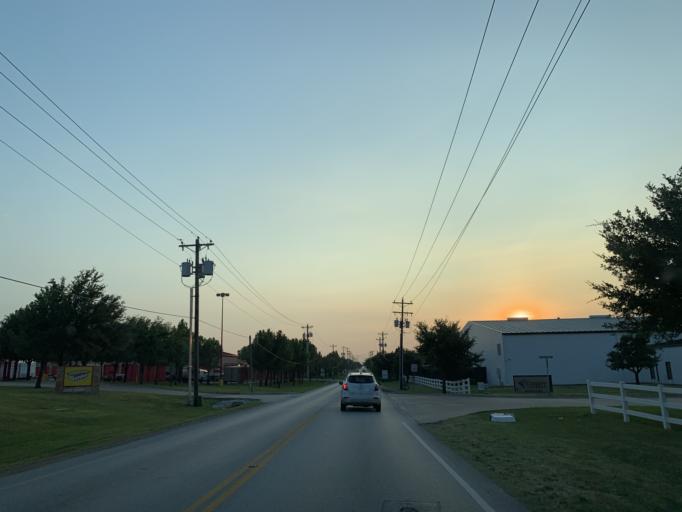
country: US
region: Texas
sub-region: Tarrant County
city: Keller
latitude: 32.9636
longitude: -97.2510
